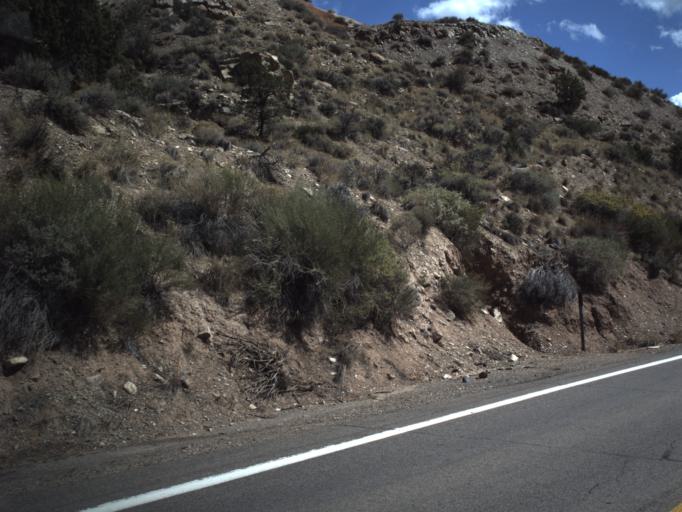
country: US
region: Utah
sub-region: Iron County
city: Cedar City
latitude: 37.6763
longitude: -113.0511
